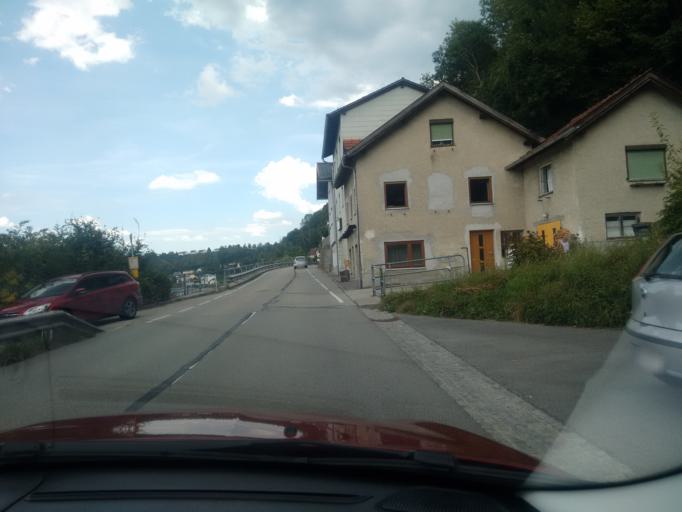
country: DE
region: Bavaria
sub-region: Upper Bavaria
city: Burghausen
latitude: 48.1512
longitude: 12.8256
